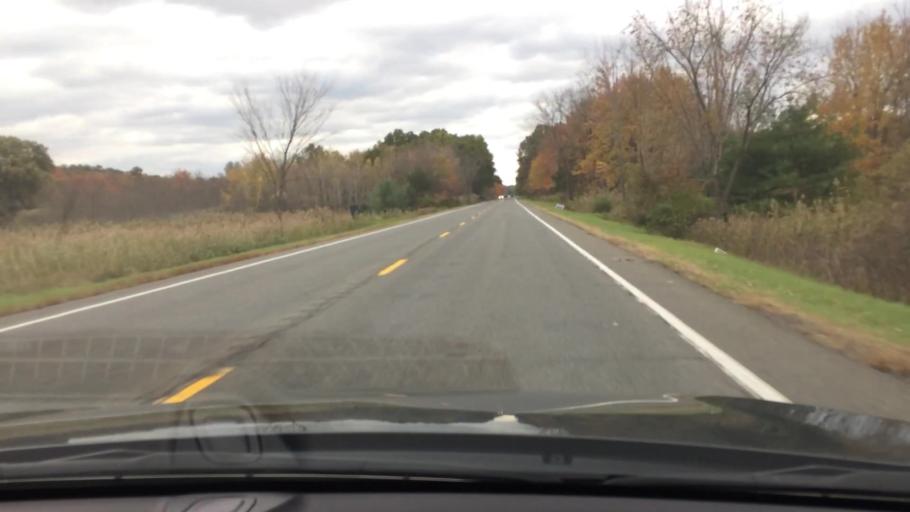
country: US
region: New York
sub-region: Columbia County
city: Kinderhook
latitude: 42.3483
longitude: -73.7050
